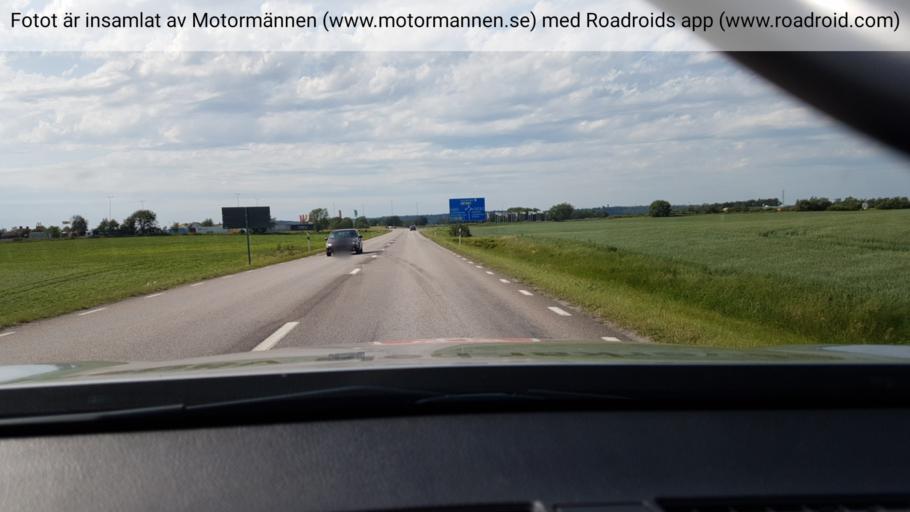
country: SE
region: Vaestra Goetaland
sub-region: Falkopings Kommun
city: Falkoeping
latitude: 58.1582
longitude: 13.5809
